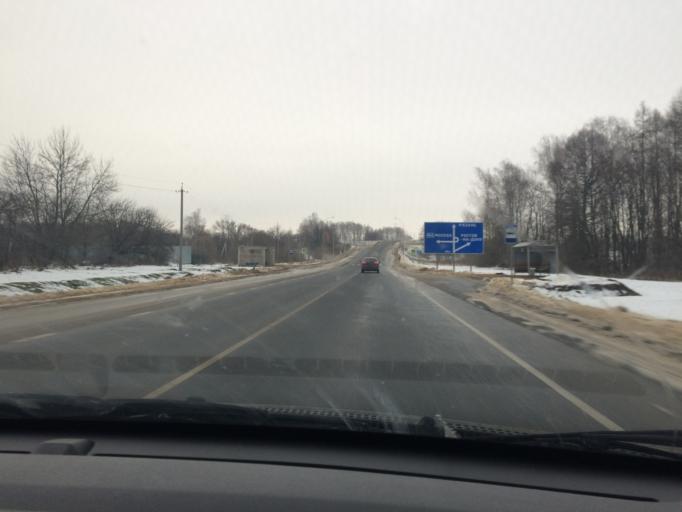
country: RU
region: Tula
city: Venev
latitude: 54.3369
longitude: 38.1437
